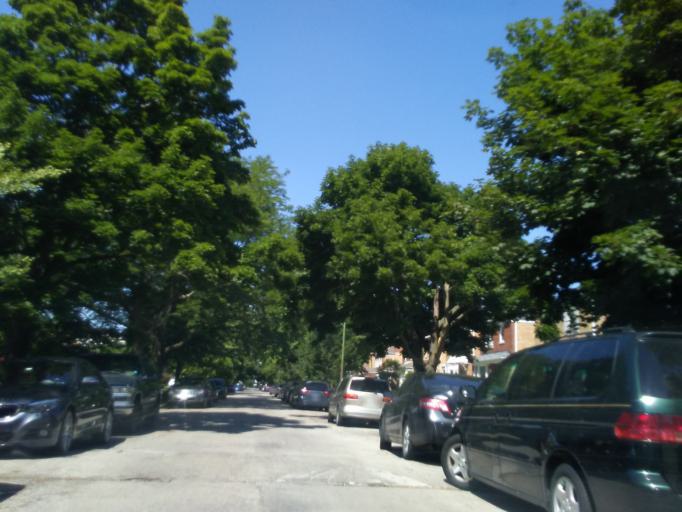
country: US
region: Illinois
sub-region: Cook County
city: Lincolnwood
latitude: 42.0174
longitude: -87.7051
